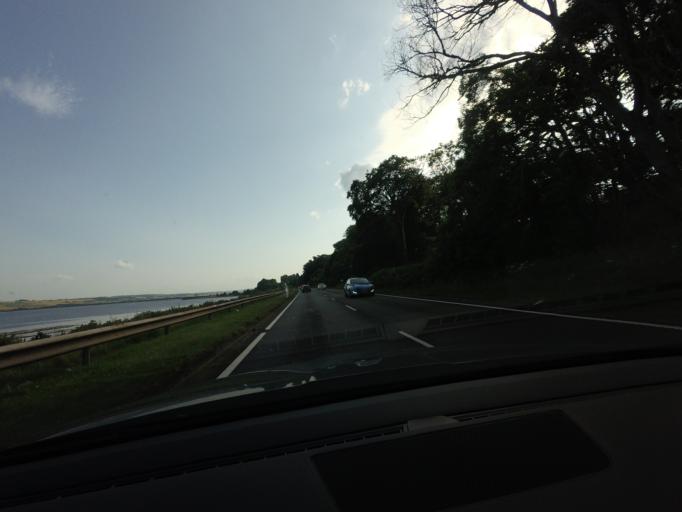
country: GB
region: Scotland
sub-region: Highland
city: Evanton
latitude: 57.6339
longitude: -4.3620
